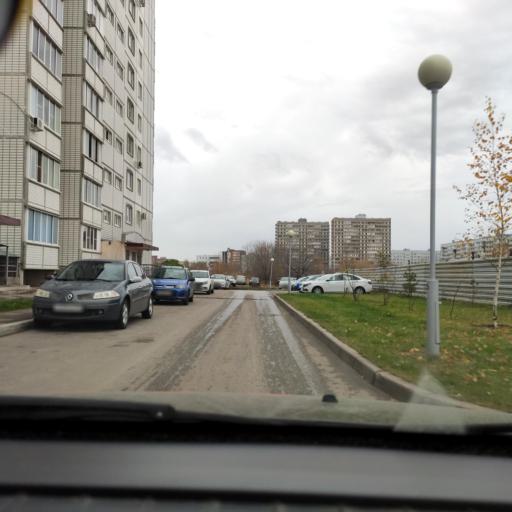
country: RU
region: Samara
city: Tol'yatti
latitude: 53.5240
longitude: 49.3334
